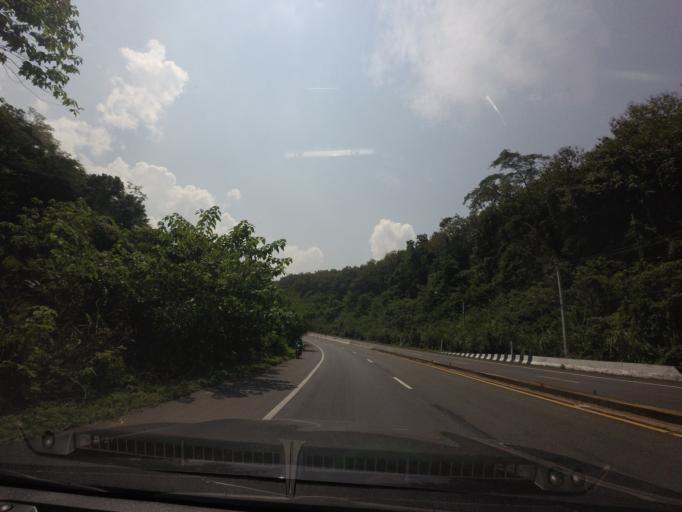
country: TH
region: Phrae
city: Den Chai
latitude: 17.8774
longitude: 100.0448
